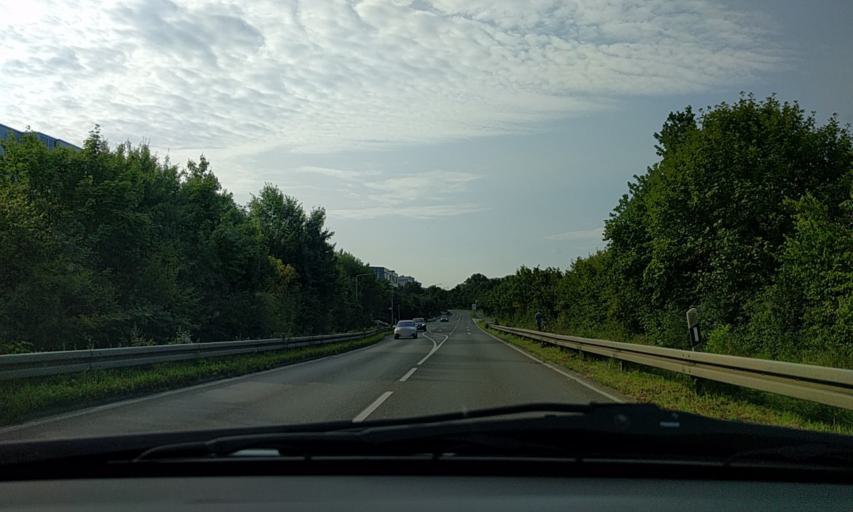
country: DE
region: North Rhine-Westphalia
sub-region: Regierungsbezirk Dusseldorf
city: Ratingen
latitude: 51.3044
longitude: 6.8381
